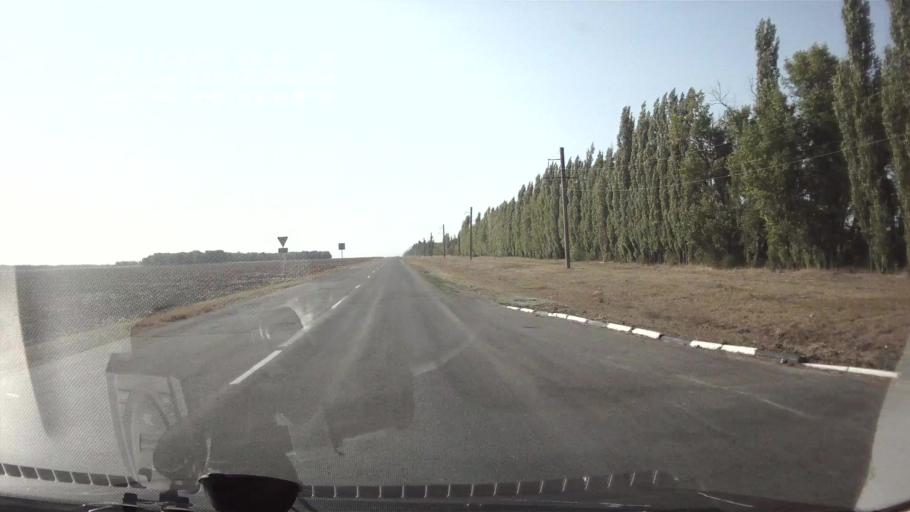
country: RU
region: Rostov
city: Tselina
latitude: 46.5348
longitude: 40.8998
